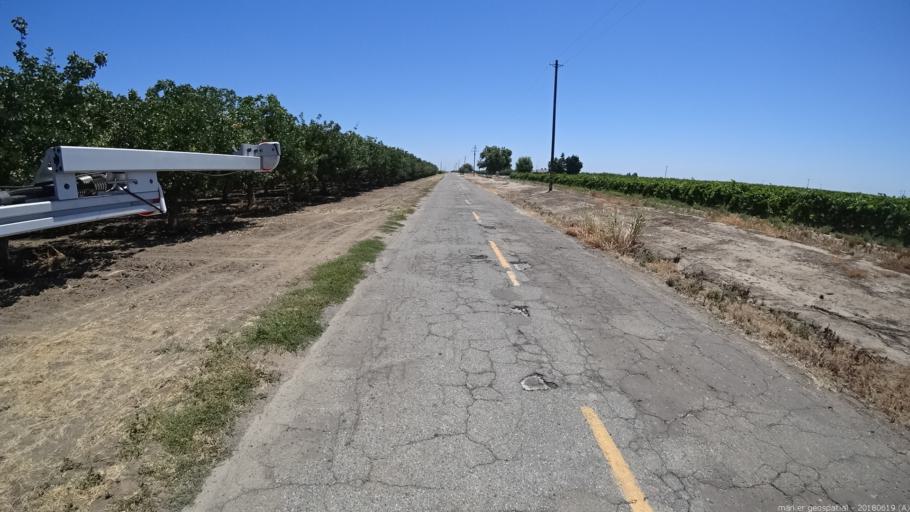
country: US
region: California
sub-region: Madera County
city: Parkwood
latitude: 36.8731
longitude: -120.0854
